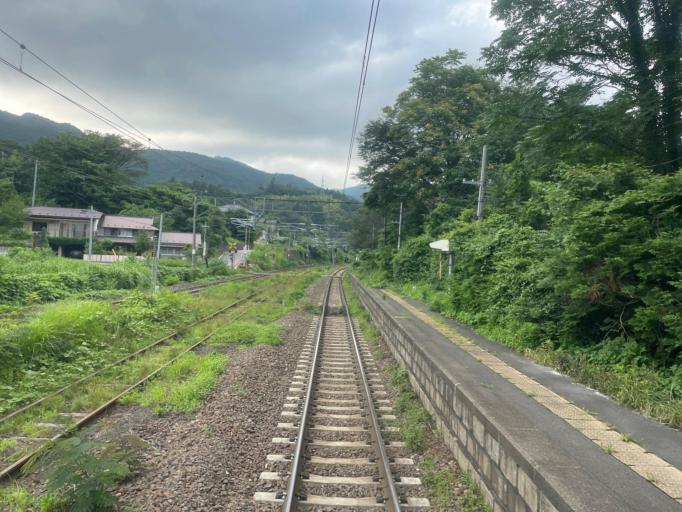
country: JP
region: Miyagi
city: Shiroishi
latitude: 37.9346
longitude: 140.6040
